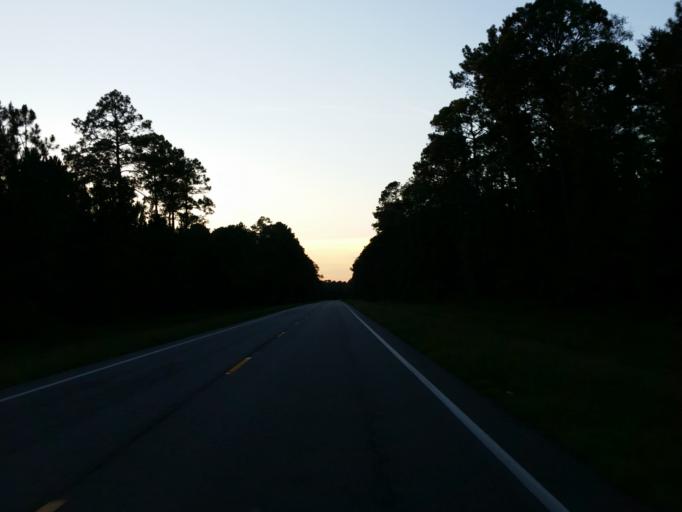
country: US
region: Georgia
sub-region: Berrien County
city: Nashville
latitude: 31.2330
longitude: -83.3071
